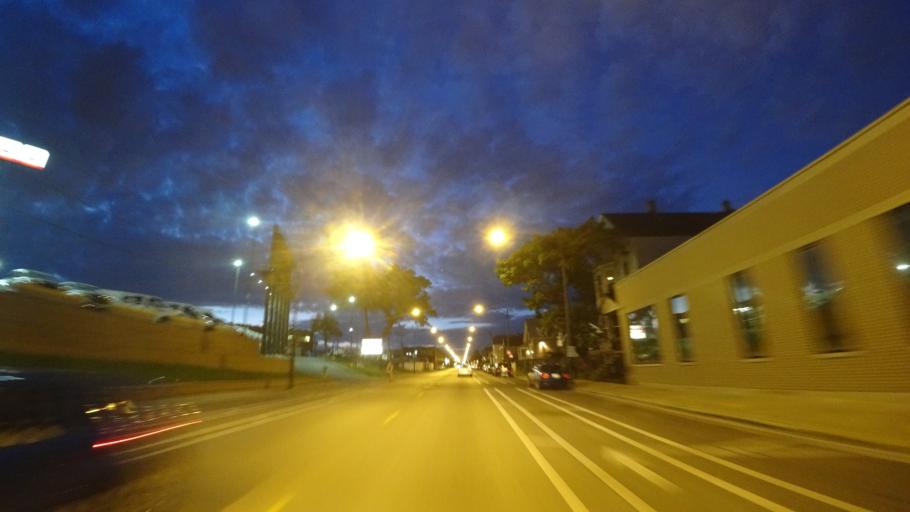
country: US
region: Illinois
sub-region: Cook County
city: Lincolnwood
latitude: 41.9402
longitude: -87.7076
